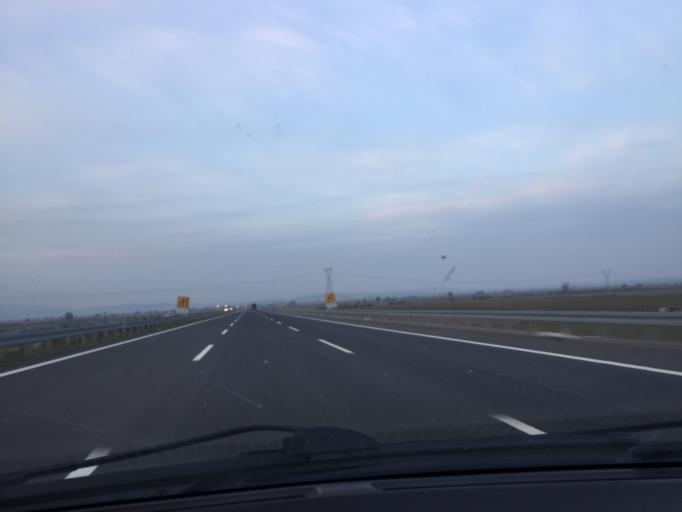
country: TR
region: Manisa
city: Halitpasa
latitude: 38.7143
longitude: 27.6489
